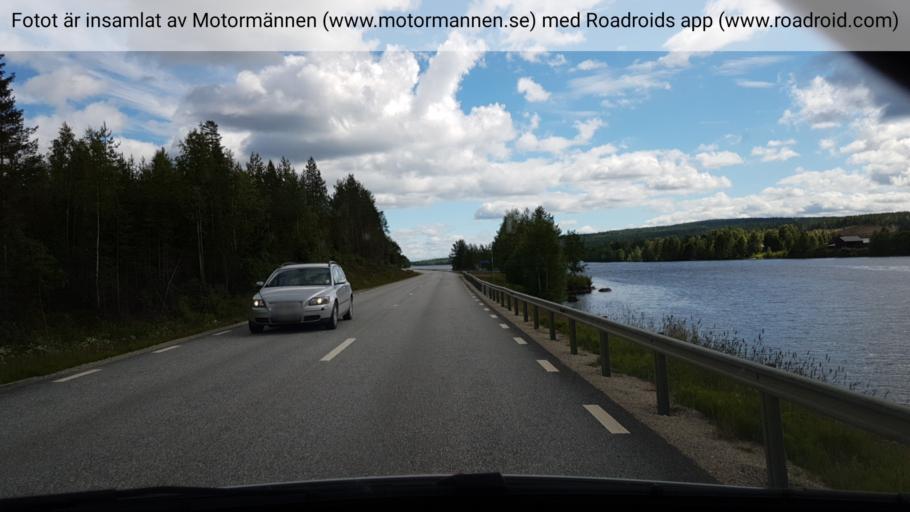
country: SE
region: Vaesterbotten
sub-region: Vindelns Kommun
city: Vindeln
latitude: 64.1803
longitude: 19.4771
